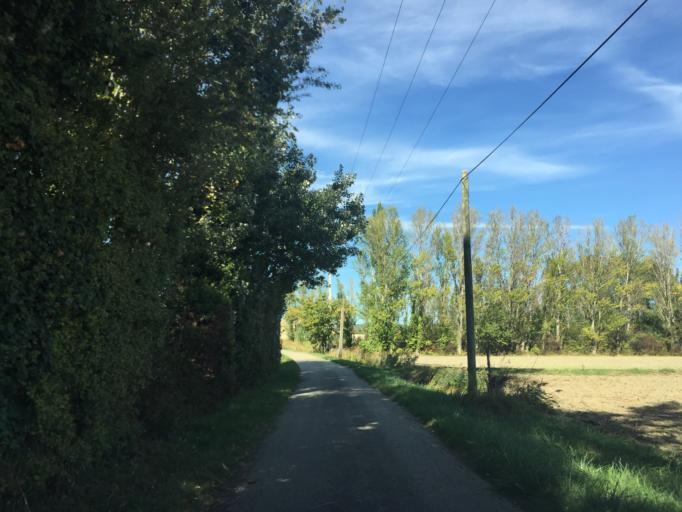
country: FR
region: Provence-Alpes-Cote d'Azur
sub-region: Departement du Vaucluse
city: Piolenc
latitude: 44.1685
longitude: 4.7370
